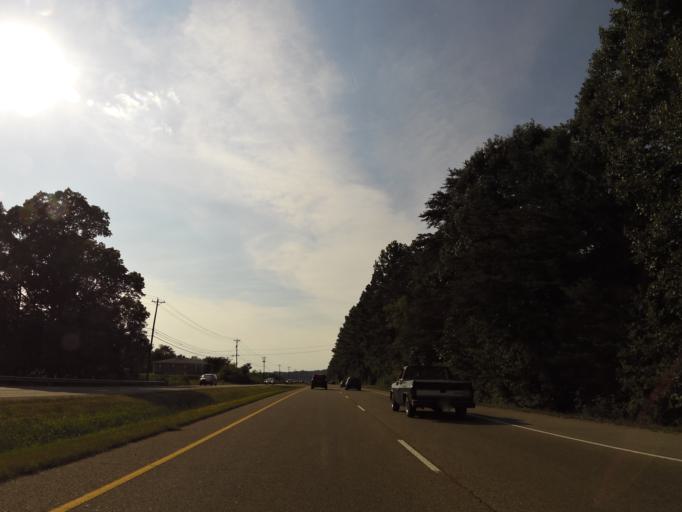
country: US
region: Tennessee
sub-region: Loudon County
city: Lenoir City
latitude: 35.8322
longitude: -84.2851
